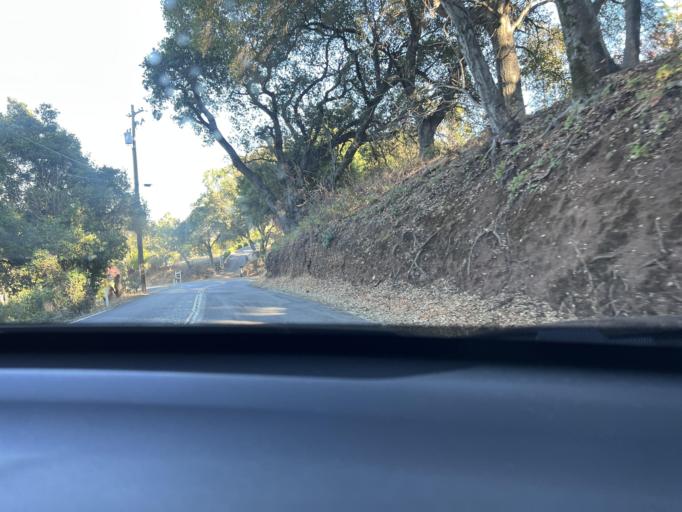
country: US
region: California
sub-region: Santa Clara County
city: Loyola
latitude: 37.2873
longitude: -122.0900
